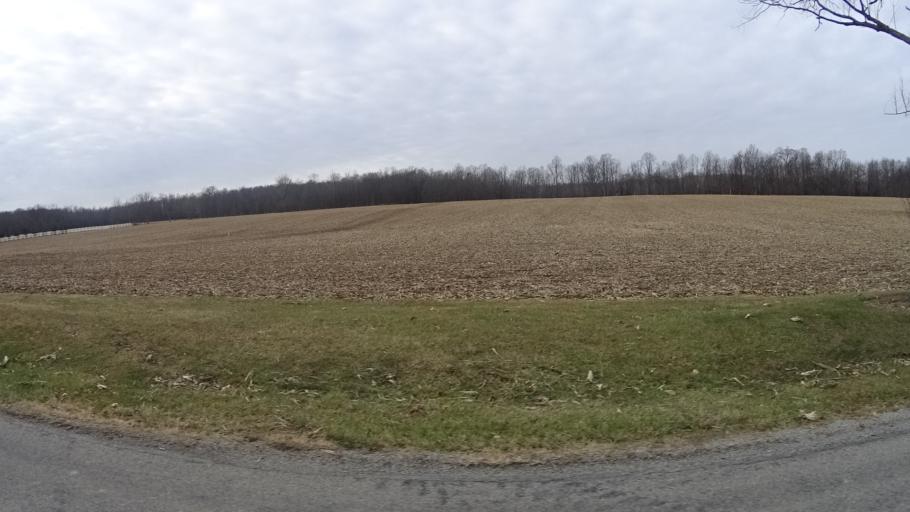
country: US
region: Ohio
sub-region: Lorain County
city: Wellington
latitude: 41.1812
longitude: -82.2424
